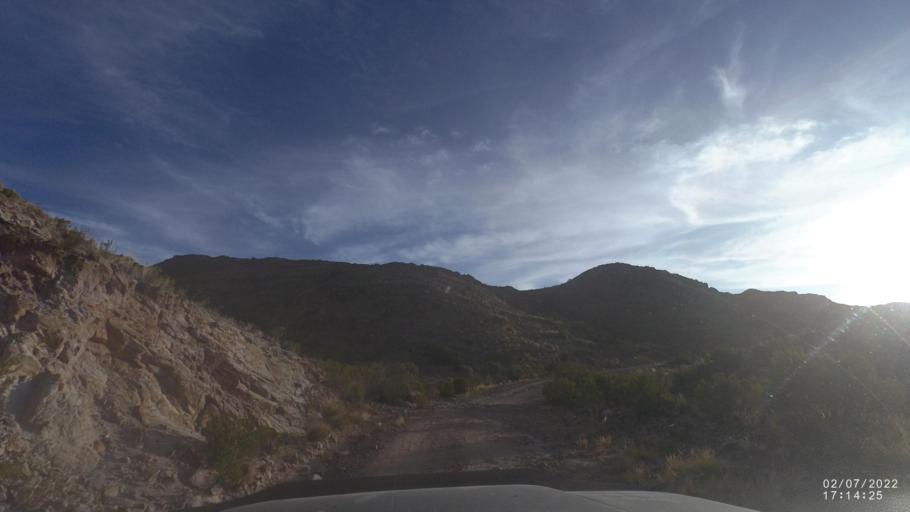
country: BO
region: Cochabamba
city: Irpa Irpa
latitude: -17.8792
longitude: -66.5807
